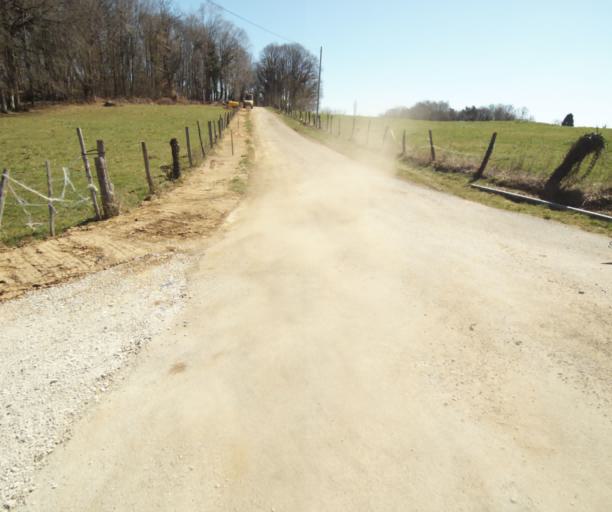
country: FR
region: Limousin
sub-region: Departement de la Correze
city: Saint-Clement
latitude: 45.3718
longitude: 1.6825
